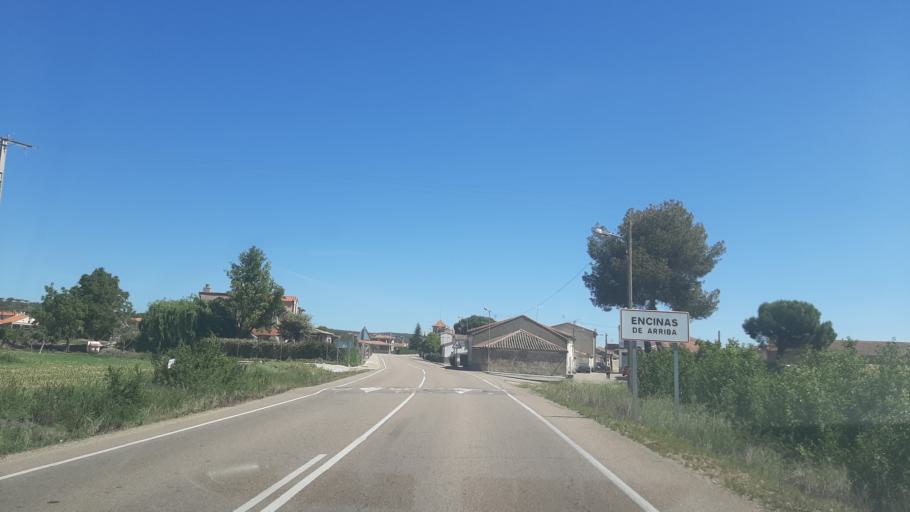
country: ES
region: Castille and Leon
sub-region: Provincia de Salamanca
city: Encinas de Arriba
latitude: 40.7690
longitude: -5.5583
